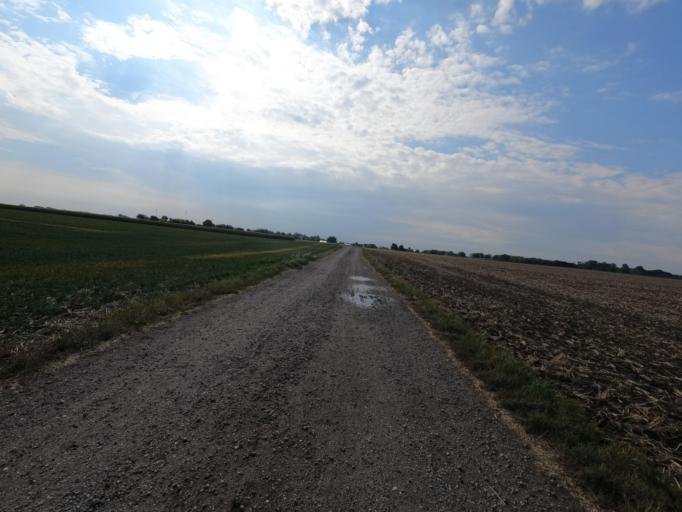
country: DE
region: North Rhine-Westphalia
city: Huckelhoven
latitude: 51.0842
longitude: 6.2125
